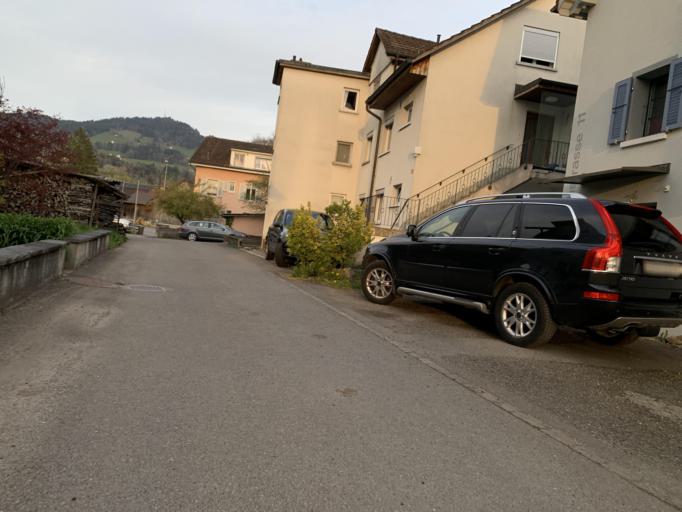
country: CH
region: Zurich
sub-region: Bezirk Hinwil
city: Hinwil
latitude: 47.2885
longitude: 8.8411
